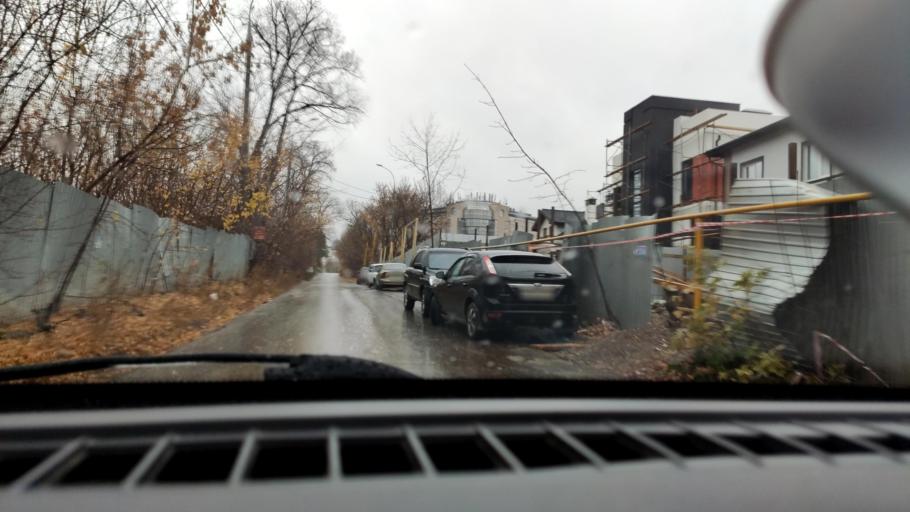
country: RU
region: Samara
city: Samara
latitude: 53.2334
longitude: 50.1752
